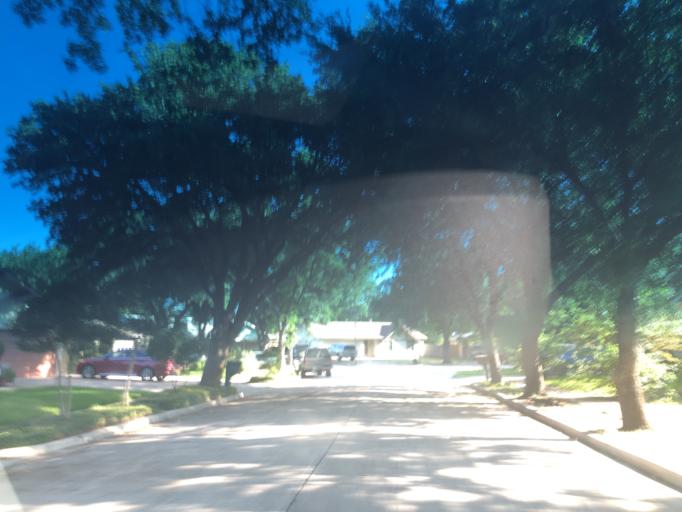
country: US
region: Texas
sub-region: Dallas County
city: Grand Prairie
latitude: 32.7062
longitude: -97.0010
